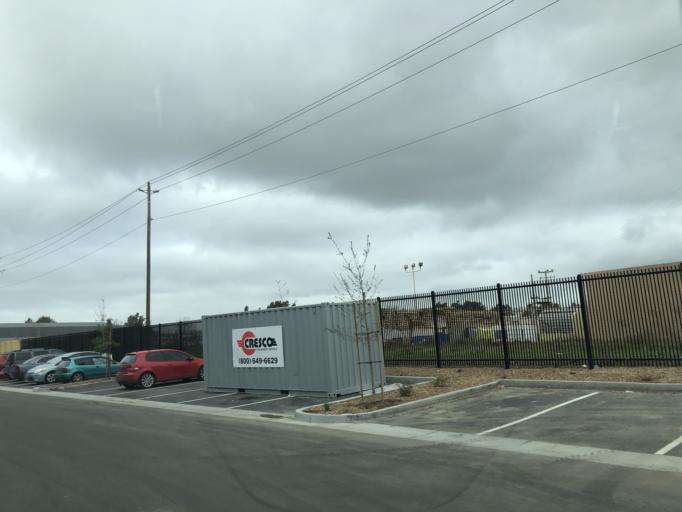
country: US
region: California
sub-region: Alameda County
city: Newark
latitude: 37.5204
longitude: -122.0306
